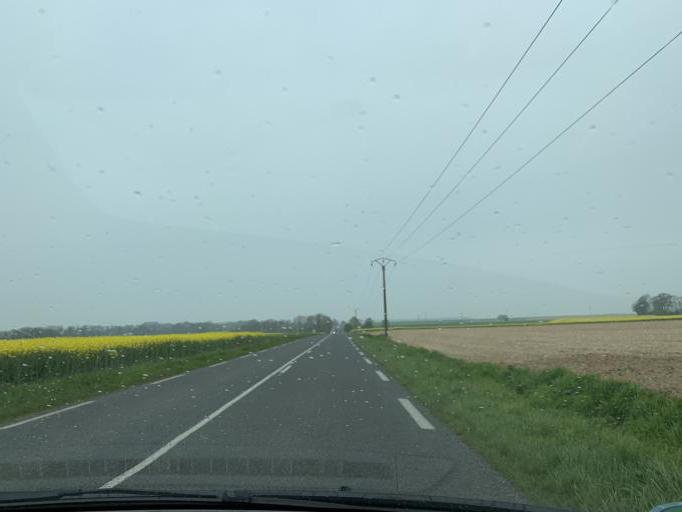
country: FR
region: Haute-Normandie
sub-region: Departement de la Seine-Maritime
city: Cany-Barville
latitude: 49.7972
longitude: 0.6642
